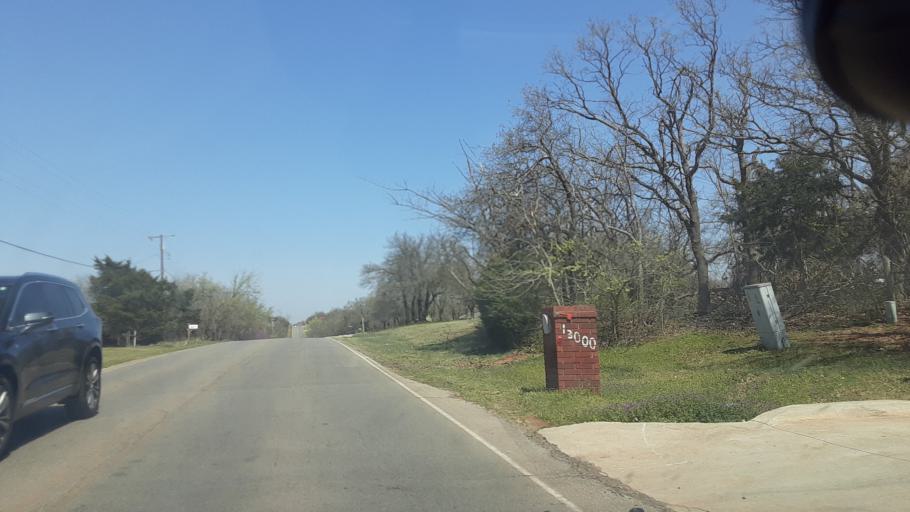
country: US
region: Oklahoma
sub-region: Oklahoma County
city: Edmond
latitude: 35.7439
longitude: -97.4784
